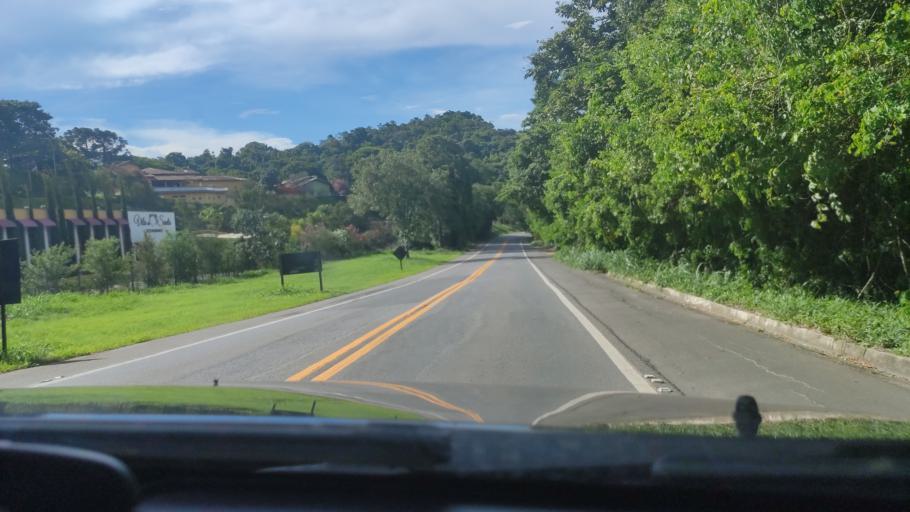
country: BR
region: Sao Paulo
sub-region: Aguas De Lindoia
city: Aguas de Lindoia
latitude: -22.5432
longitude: -46.6271
